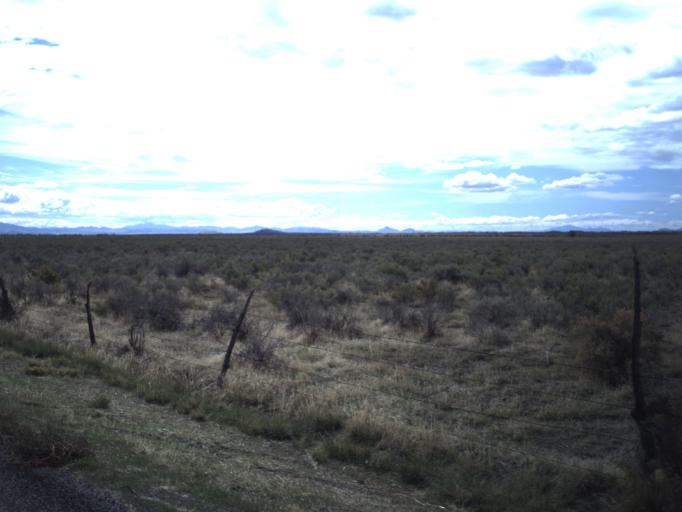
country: US
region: Utah
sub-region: Millard County
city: Fillmore
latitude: 39.0808
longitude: -112.4099
